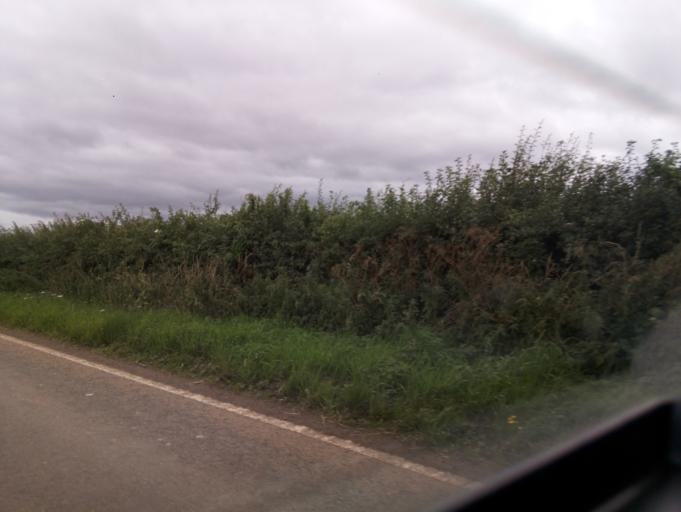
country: GB
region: England
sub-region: Worcestershire
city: Kempsey
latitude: 52.1173
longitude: -2.2224
